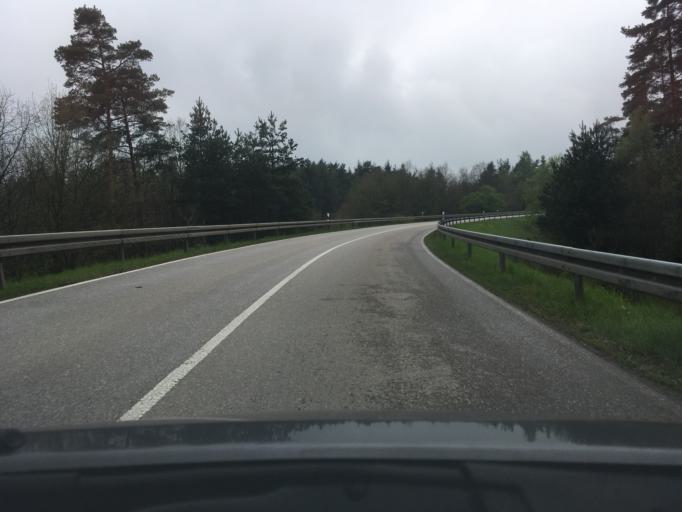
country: DE
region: Bavaria
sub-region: Upper Palatinate
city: Burglengenfeld
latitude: 49.1928
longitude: 12.0601
